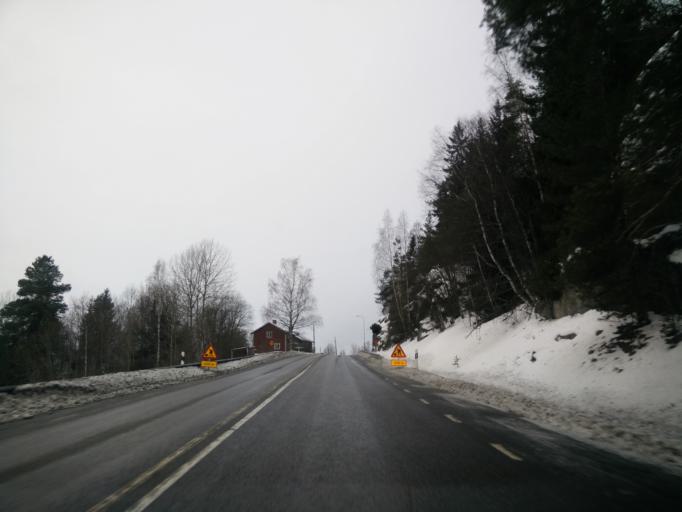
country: SE
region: Vaesternorrland
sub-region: Sundsvalls Kommun
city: Matfors
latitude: 62.4175
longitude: 16.6217
